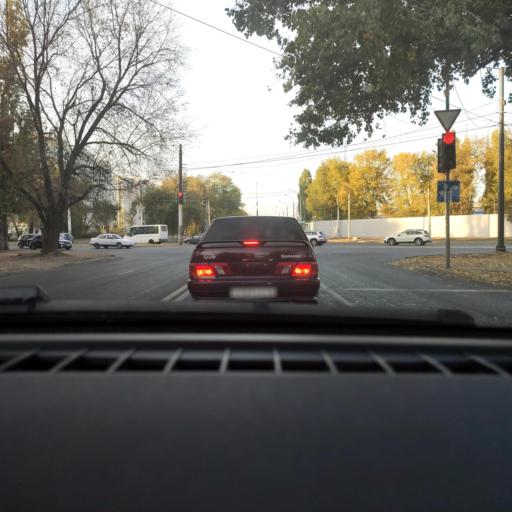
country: RU
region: Voronezj
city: Maslovka
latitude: 51.5998
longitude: 39.2438
